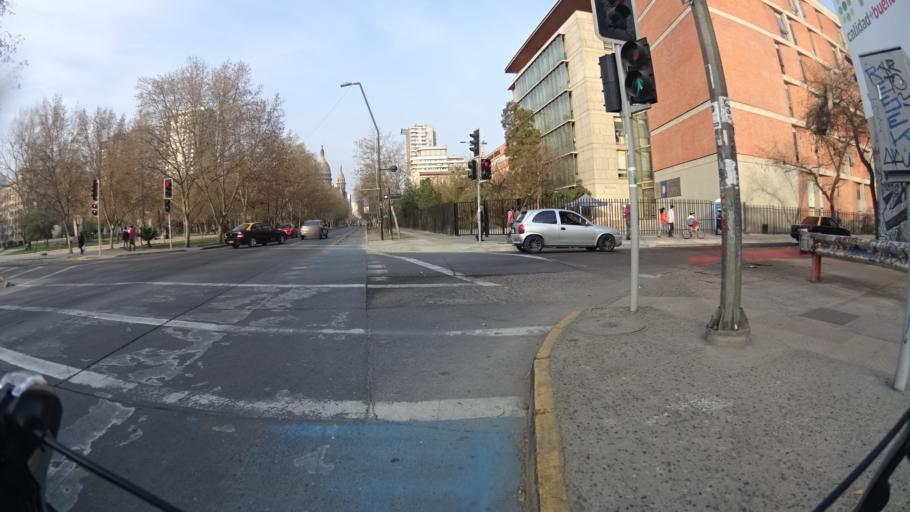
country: CL
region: Santiago Metropolitan
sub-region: Provincia de Santiago
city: Santiago
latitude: -33.4526
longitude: -70.6530
